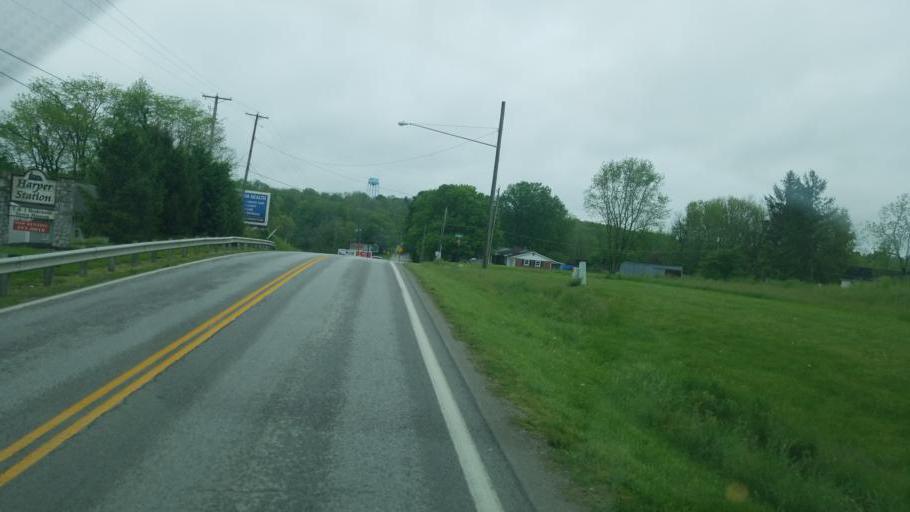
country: US
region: Ohio
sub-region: Highland County
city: Hillsboro
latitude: 39.2186
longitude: -83.6175
